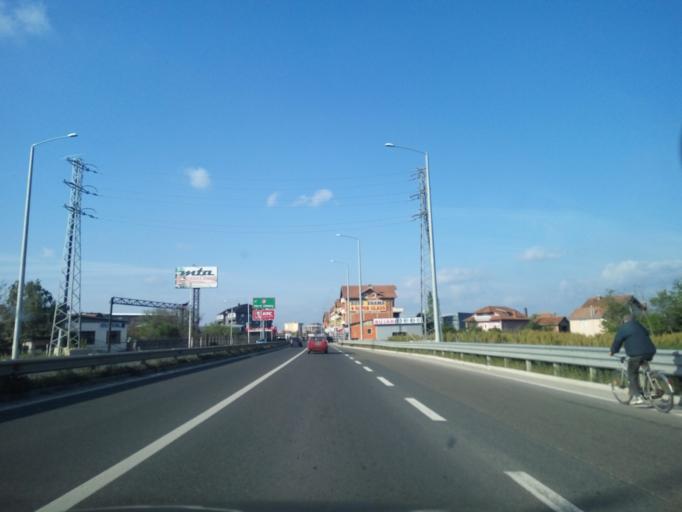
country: XK
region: Pristina
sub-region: Kosovo Polje
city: Kosovo Polje
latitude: 42.6247
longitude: 21.0861
